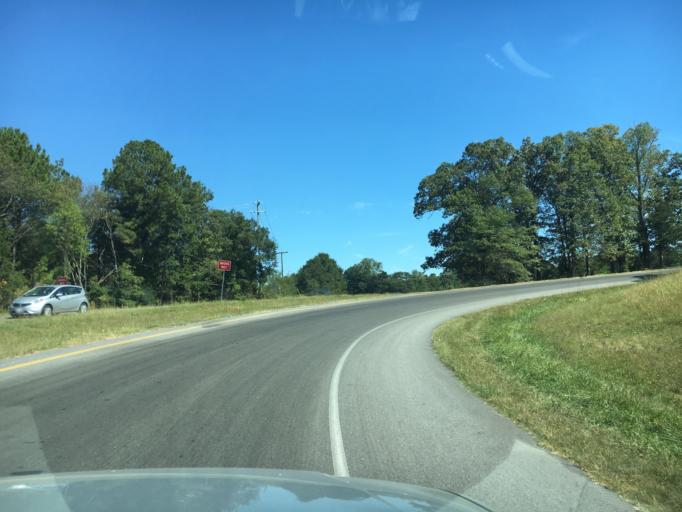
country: US
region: South Carolina
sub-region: Spartanburg County
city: Wellford
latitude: 34.9406
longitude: -82.0760
